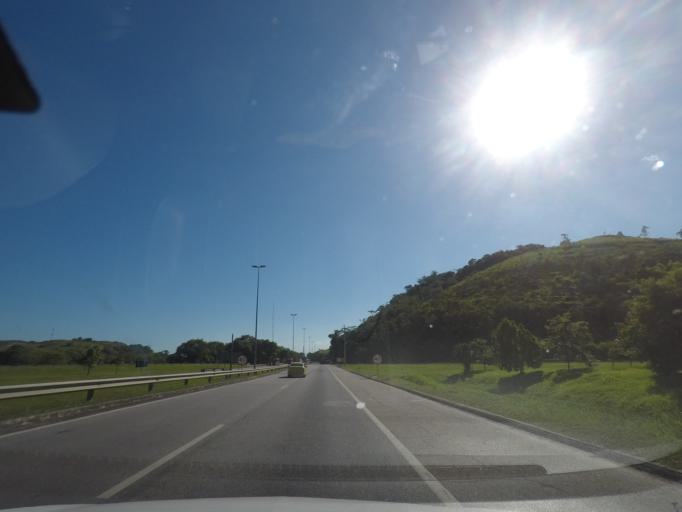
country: BR
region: Rio de Janeiro
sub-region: Guapimirim
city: Guapimirim
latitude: -22.6572
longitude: -43.0893
